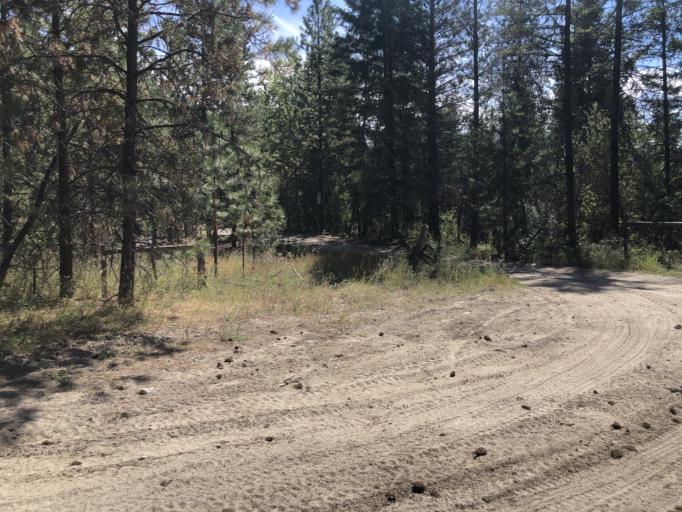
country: CA
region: British Columbia
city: Summerland
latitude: 49.6300
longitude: -119.5613
